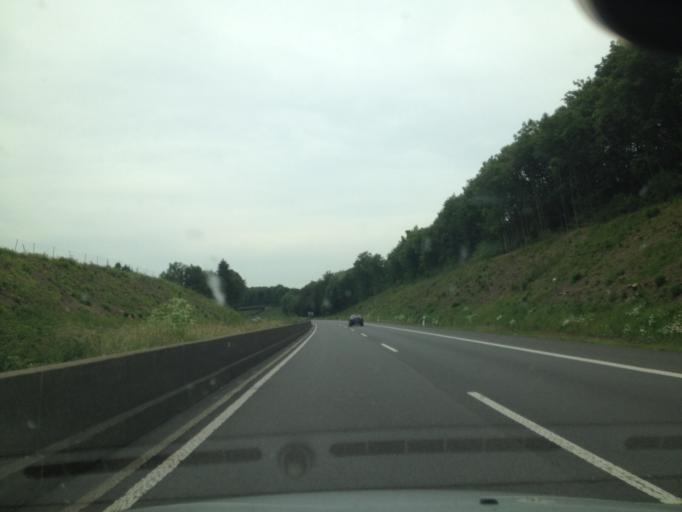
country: DE
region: North Rhine-Westphalia
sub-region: Regierungsbezirk Arnsberg
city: Drolshagen
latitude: 50.9742
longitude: 7.7403
